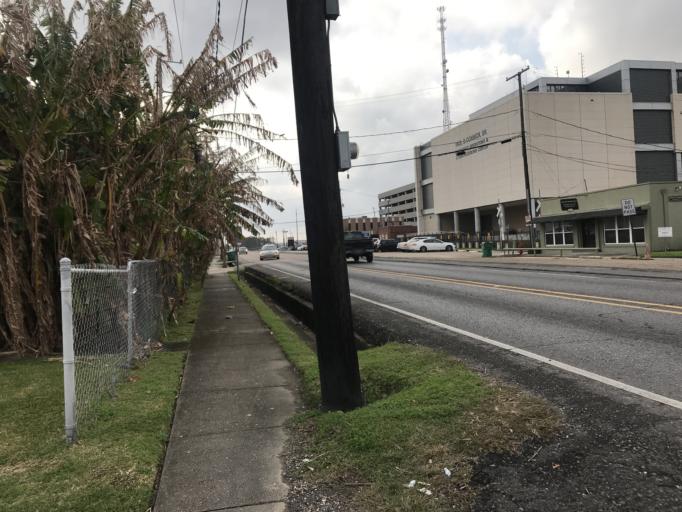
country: US
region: Louisiana
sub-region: Jefferson Parish
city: Gretna
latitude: 29.9153
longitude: -90.0651
